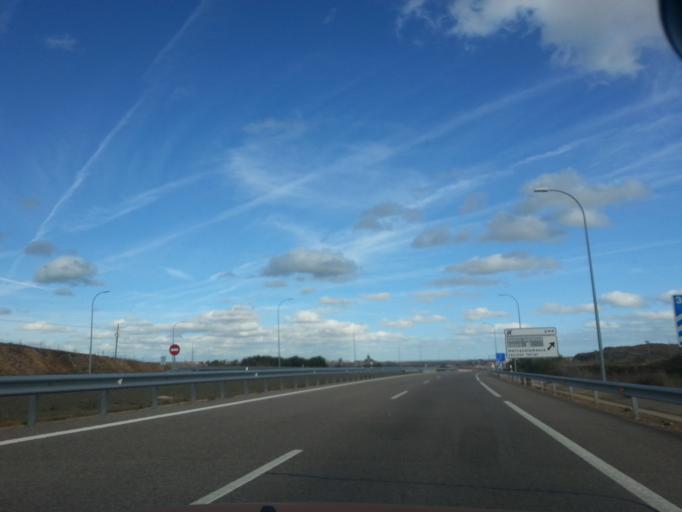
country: ES
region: Castille and Leon
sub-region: Provincia de Salamanca
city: Doninos de Salamanca
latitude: 40.9570
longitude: -5.7209
